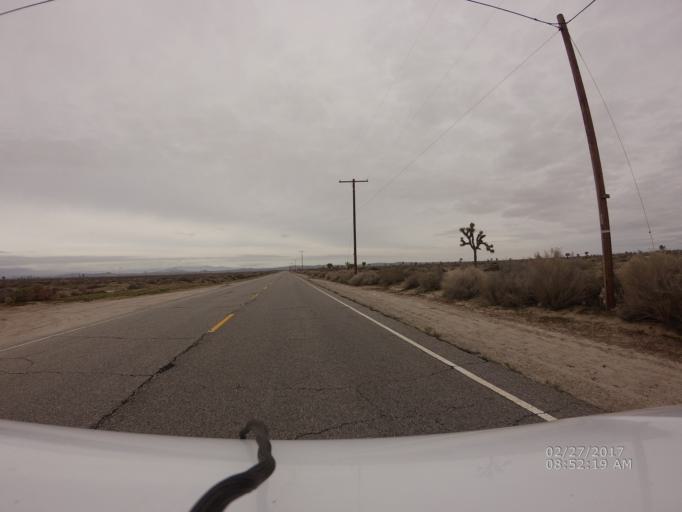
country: US
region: California
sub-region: Los Angeles County
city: Lancaster
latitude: 34.7554
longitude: -118.0772
